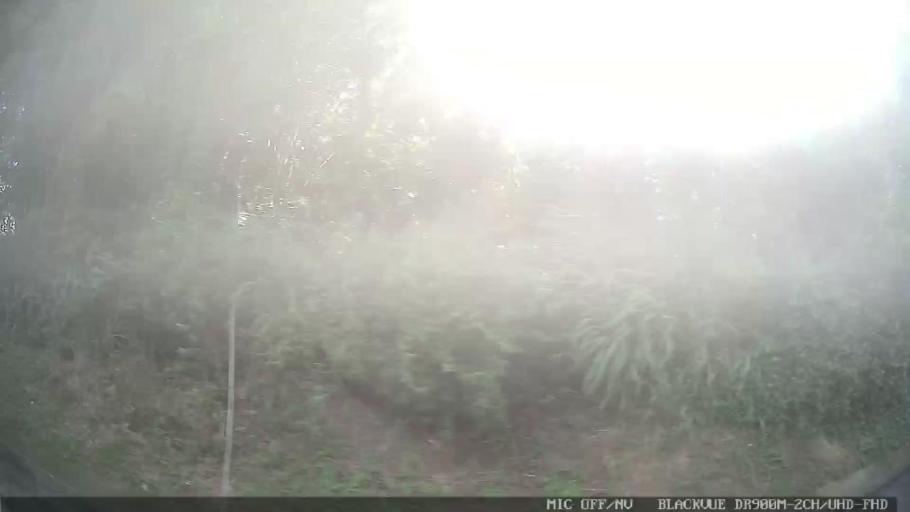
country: BR
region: Sao Paulo
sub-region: Tiete
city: Tiete
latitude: -23.1387
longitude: -47.6815
